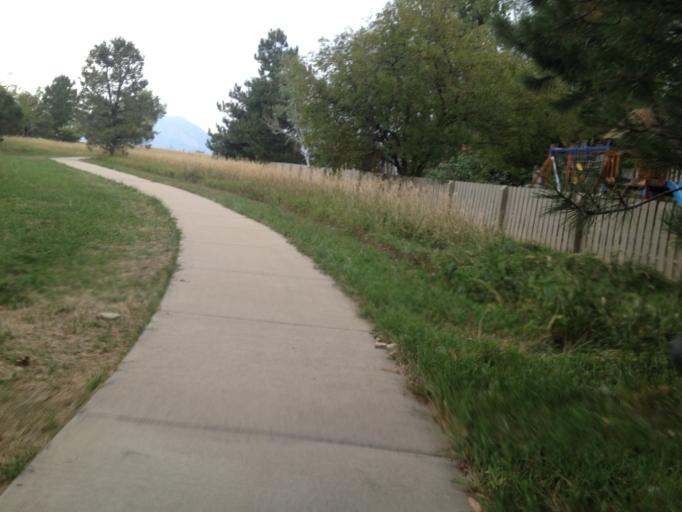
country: US
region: Colorado
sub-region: Boulder County
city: Louisville
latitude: 39.9804
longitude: -105.1581
